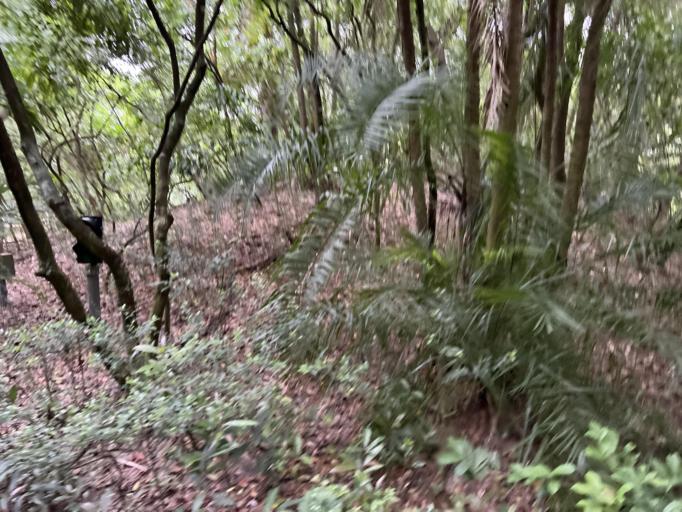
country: US
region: Florida
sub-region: Polk County
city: Citrus Ridge
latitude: 28.3656
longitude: -81.5956
